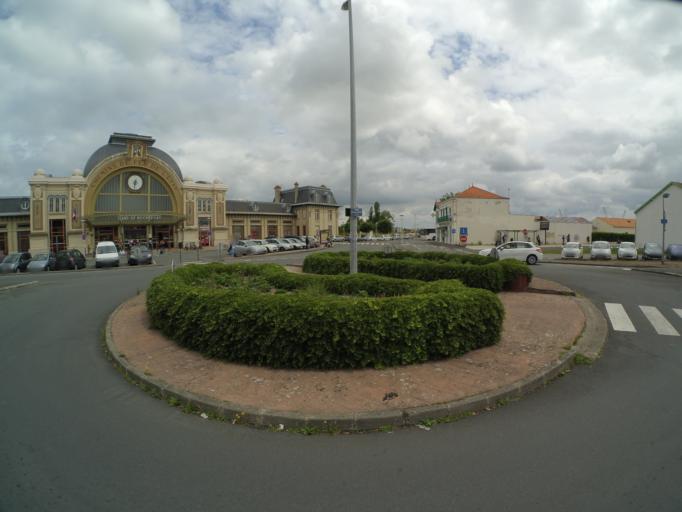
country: FR
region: Poitou-Charentes
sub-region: Departement de la Charente-Maritime
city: Rochefort
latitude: 45.9467
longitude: -0.9636
